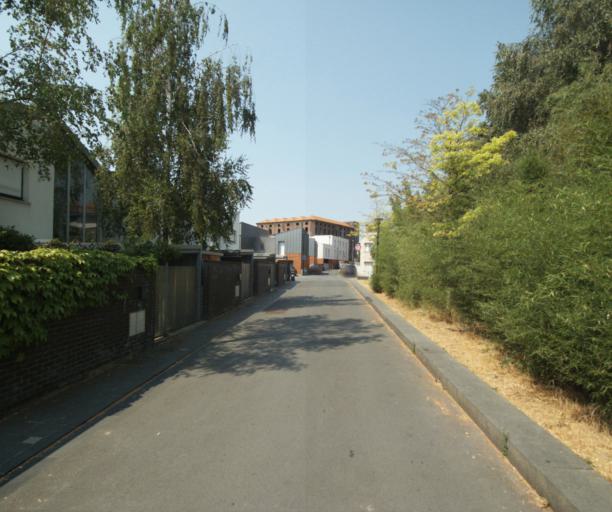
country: FR
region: Nord-Pas-de-Calais
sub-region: Departement du Nord
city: Tourcoing
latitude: 50.7207
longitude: 3.1450
